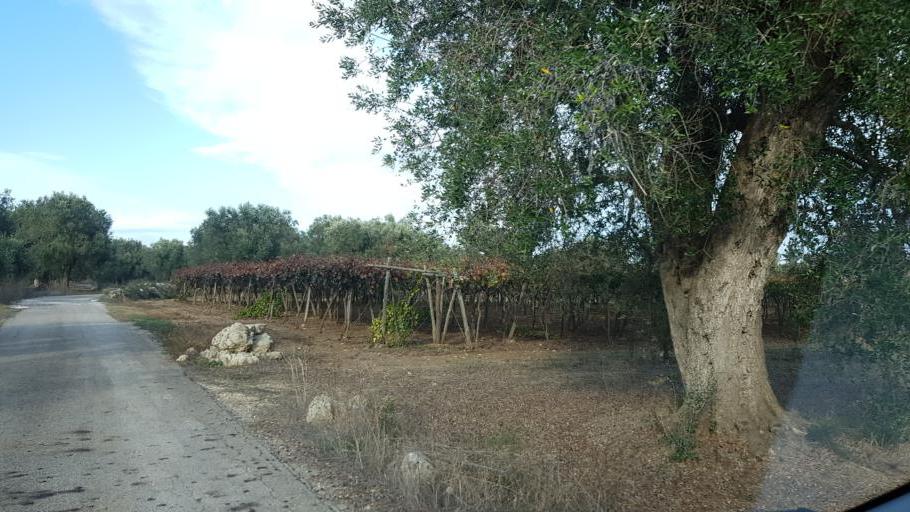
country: IT
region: Apulia
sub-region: Provincia di Brindisi
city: Oria
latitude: 40.5032
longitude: 17.6714
